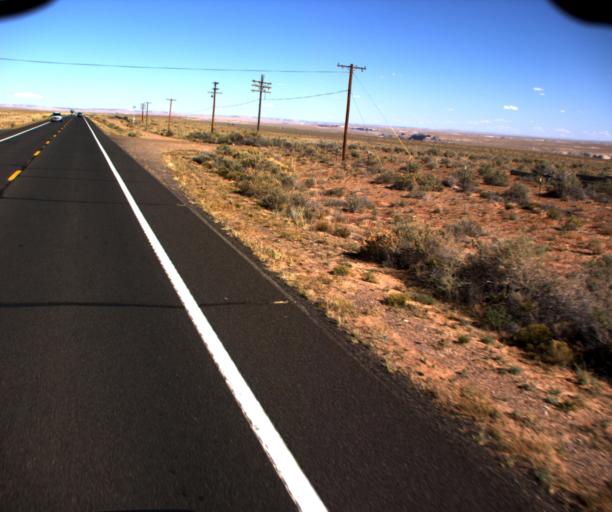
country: US
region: Arizona
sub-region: Coconino County
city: Tuba City
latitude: 36.1494
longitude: -111.1371
